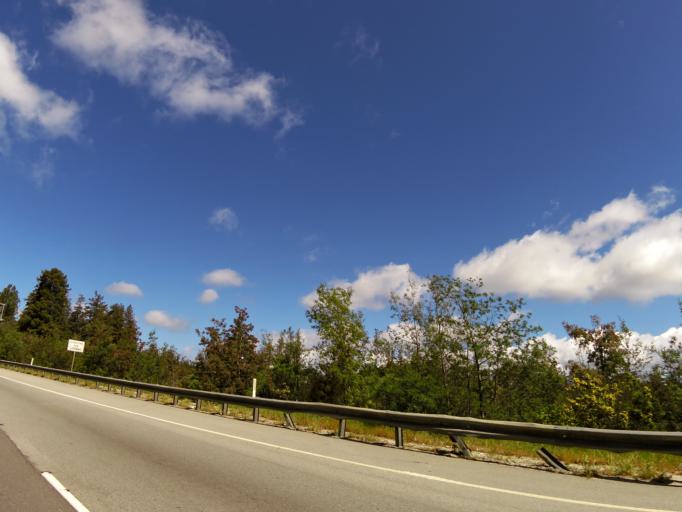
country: US
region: California
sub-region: Santa Cruz County
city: Pasatiempo
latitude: 36.9952
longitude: -122.0191
